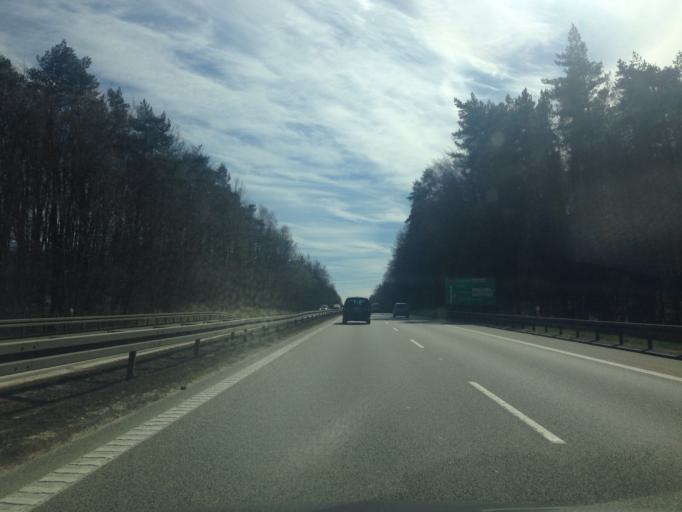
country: PL
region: Pomeranian Voivodeship
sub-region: Gdynia
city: Wielki Kack
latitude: 54.4440
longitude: 18.4905
